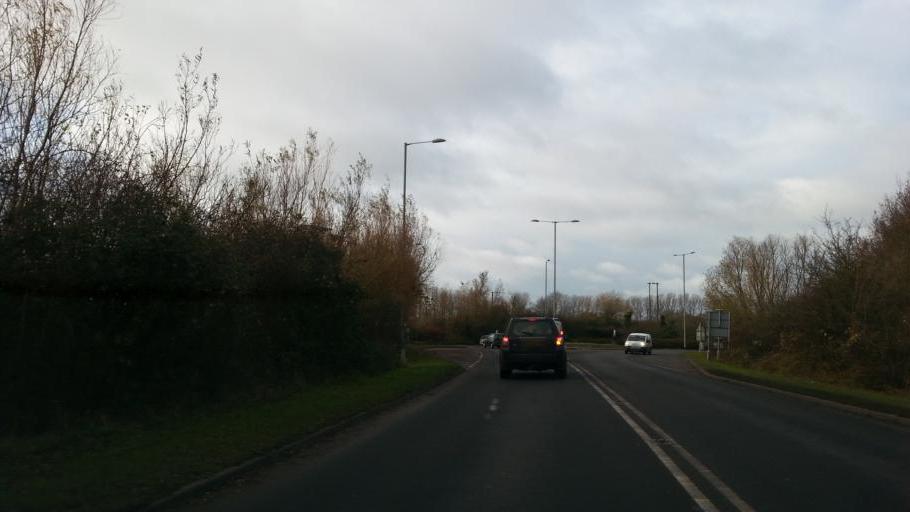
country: GB
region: England
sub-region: Norfolk
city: Downham Market
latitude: 52.5992
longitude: 0.3634
